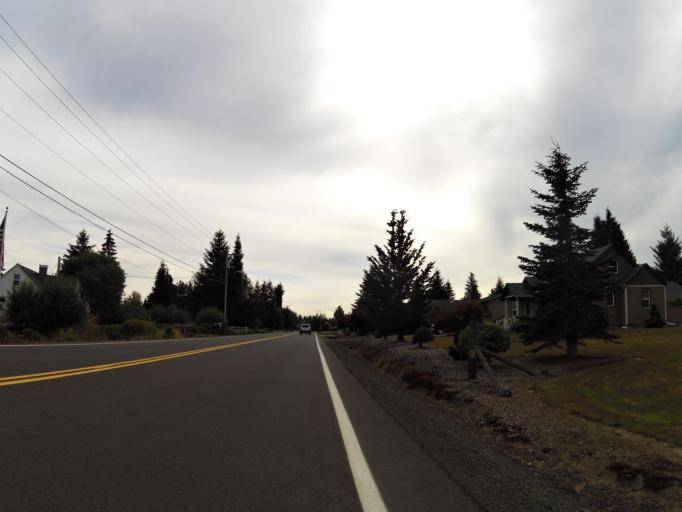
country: US
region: Washington
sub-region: Cowlitz County
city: Castle Rock
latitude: 46.2280
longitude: -122.8929
